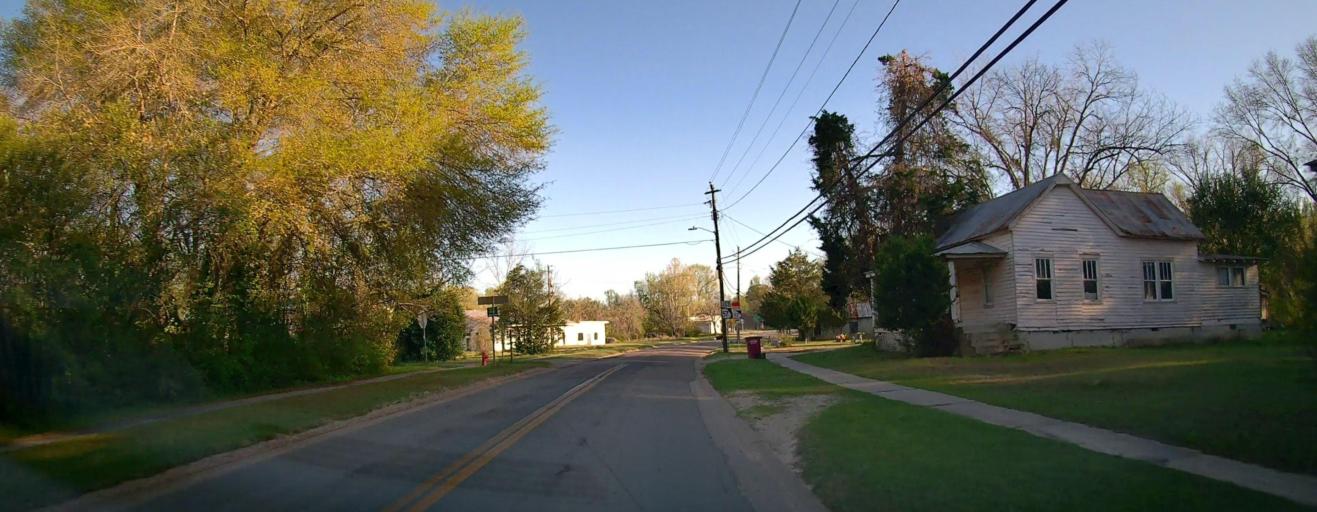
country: US
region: Georgia
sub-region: Wilkinson County
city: Irwinton
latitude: 32.8237
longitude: -83.0791
